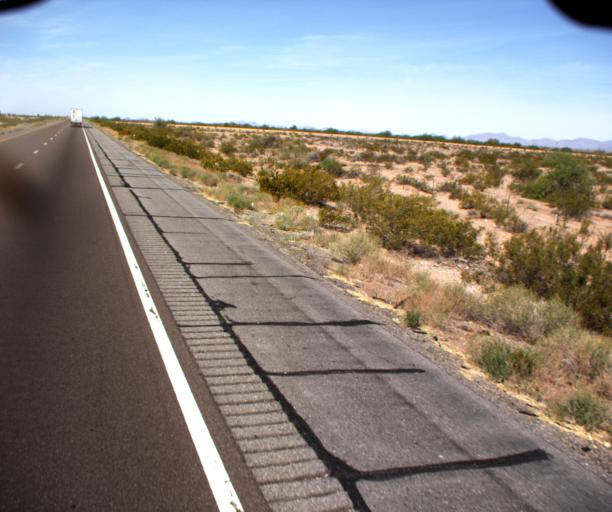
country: US
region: Arizona
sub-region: La Paz County
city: Salome
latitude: 33.5513
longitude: -113.2342
